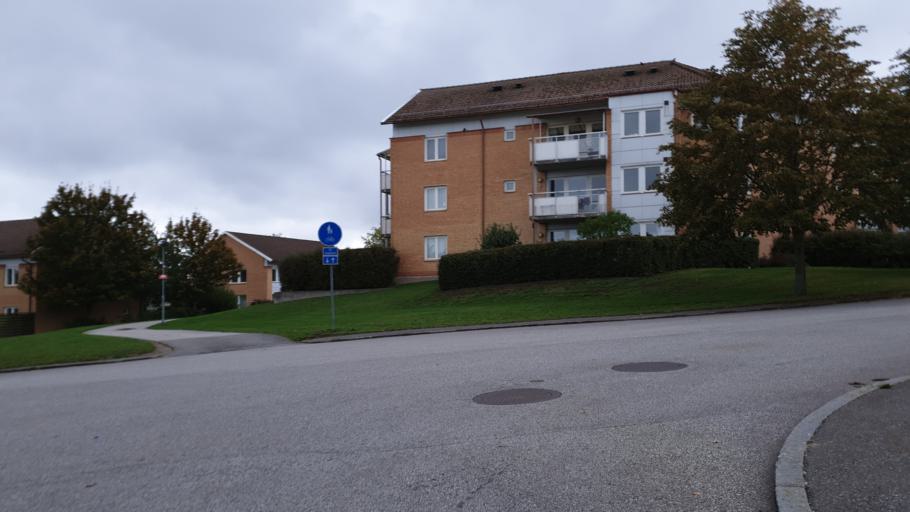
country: SE
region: Skane
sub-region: Lunds Kommun
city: Lund
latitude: 55.7124
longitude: 13.2421
